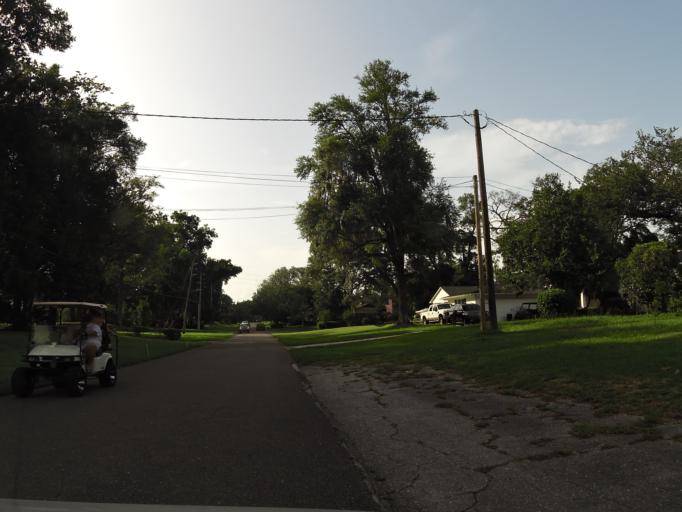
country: US
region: Florida
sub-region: Clay County
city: Bellair-Meadowbrook Terrace
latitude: 30.2600
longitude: -81.7110
